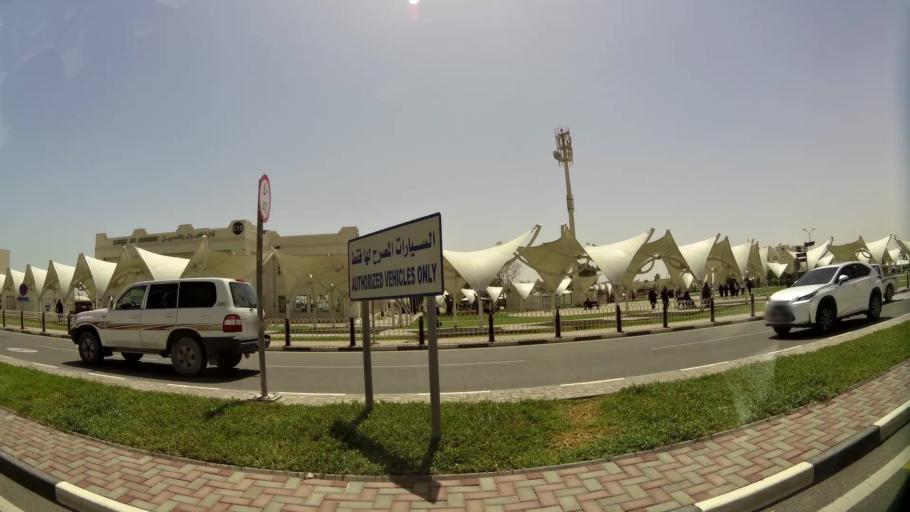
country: QA
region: Baladiyat Umm Salal
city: Umm Salal Muhammad
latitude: 25.3766
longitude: 51.4870
